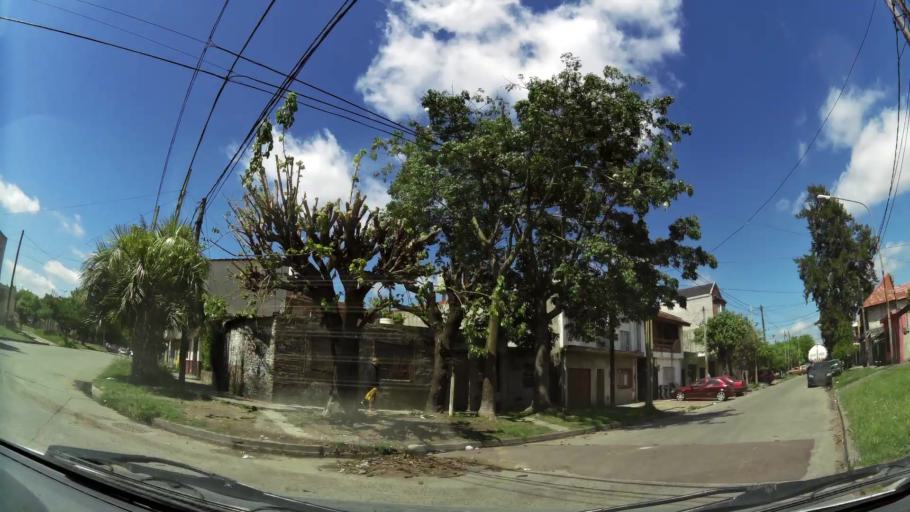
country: AR
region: Buenos Aires
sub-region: Partido de Lanus
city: Lanus
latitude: -34.6917
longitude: -58.4311
